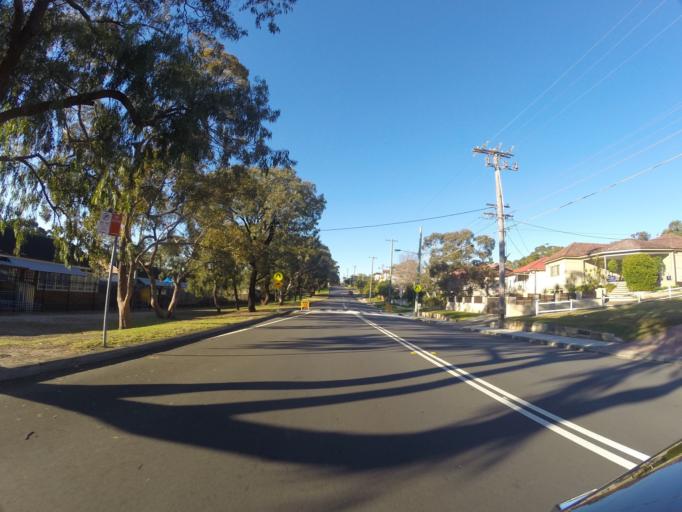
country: AU
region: New South Wales
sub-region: Sutherland Shire
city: Miranda
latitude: -34.0476
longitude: 151.1019
